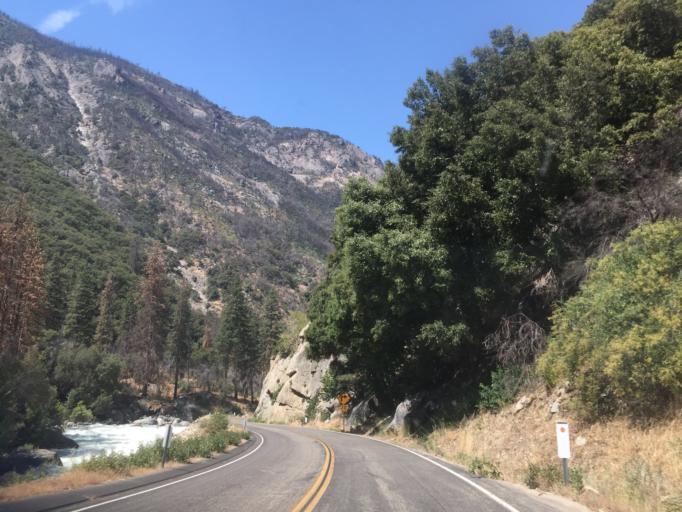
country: US
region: California
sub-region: Tulare County
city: Three Rivers
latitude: 36.8083
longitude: -118.7810
